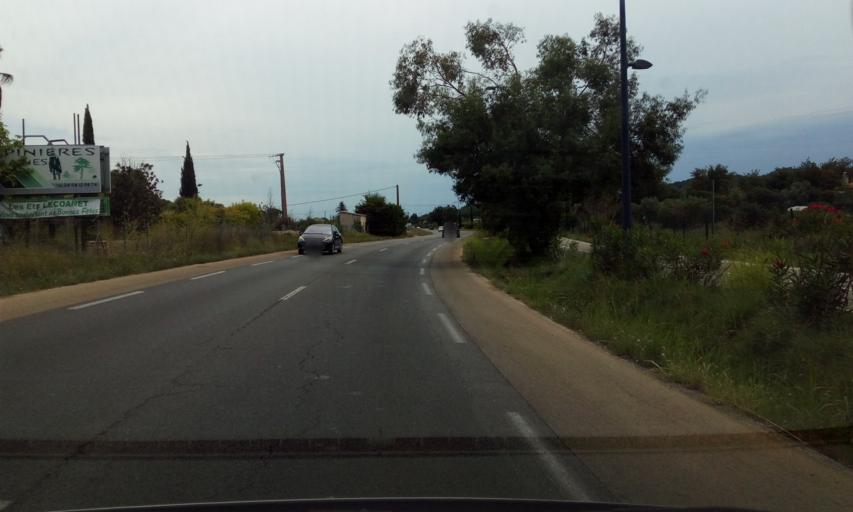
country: FR
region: Provence-Alpes-Cote d'Azur
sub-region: Departement du Var
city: Carqueiranne
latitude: 43.1067
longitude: 6.0513
